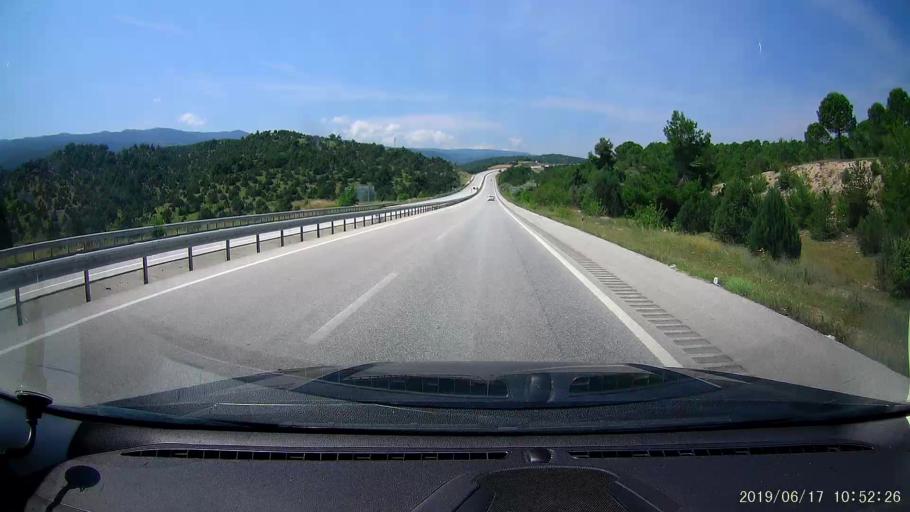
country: TR
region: Corum
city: Hacihamza
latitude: 41.0894
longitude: 34.3423
